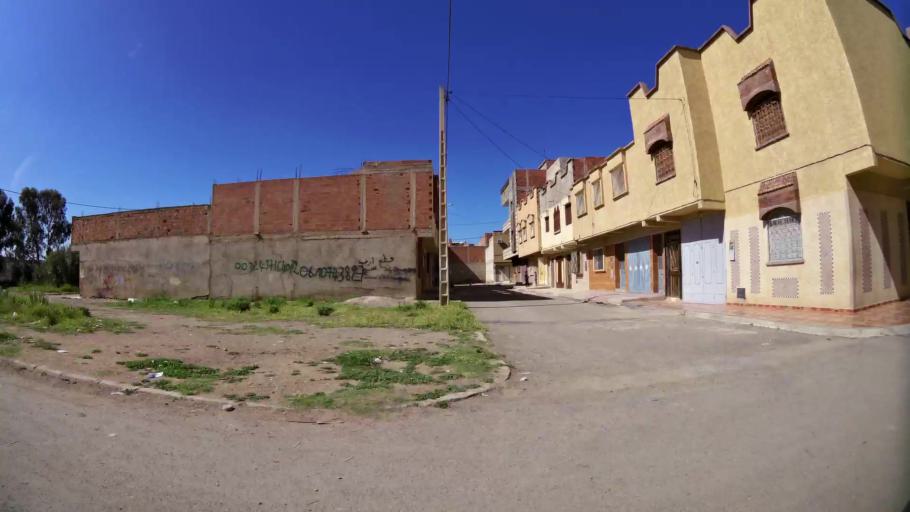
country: MA
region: Oriental
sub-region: Oujda-Angad
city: Oujda
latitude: 34.6538
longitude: -1.9339
